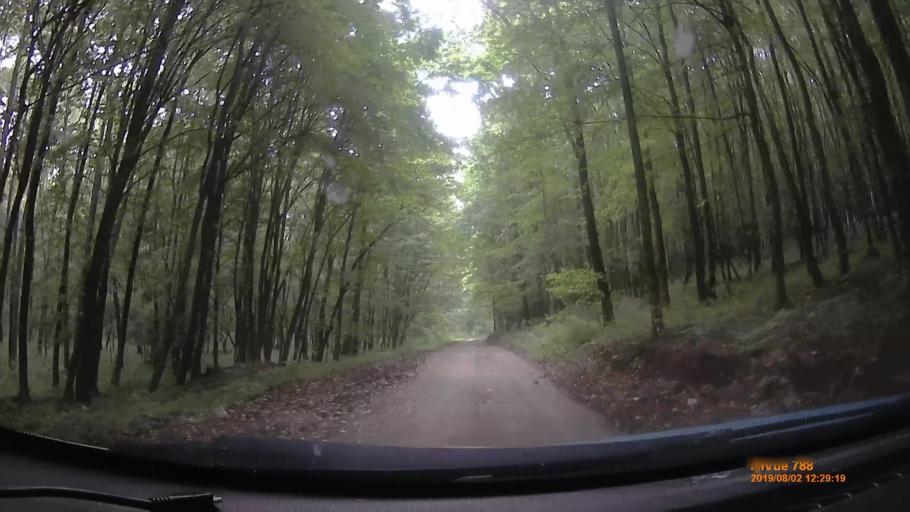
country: HU
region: Baranya
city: Buekkoesd
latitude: 46.1126
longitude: 17.9356
